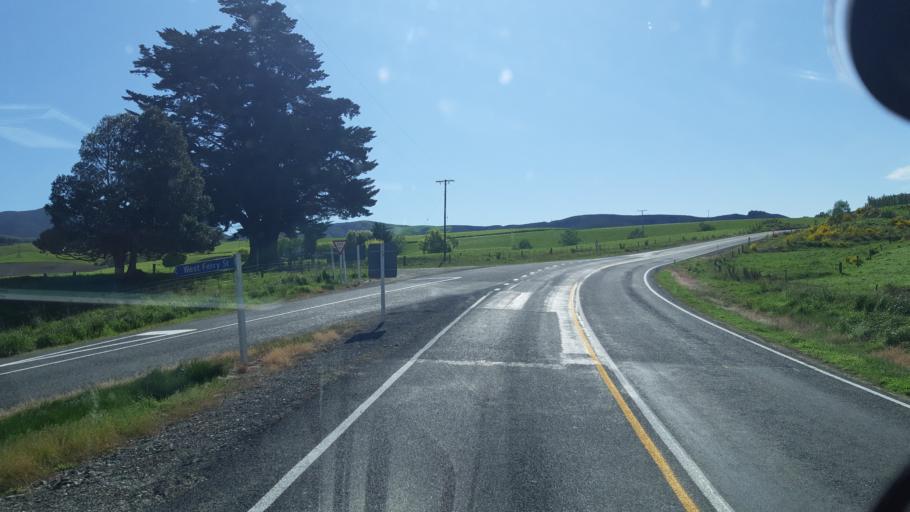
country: NZ
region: Otago
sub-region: Clutha District
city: Balclutha
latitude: -45.8174
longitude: 169.5187
